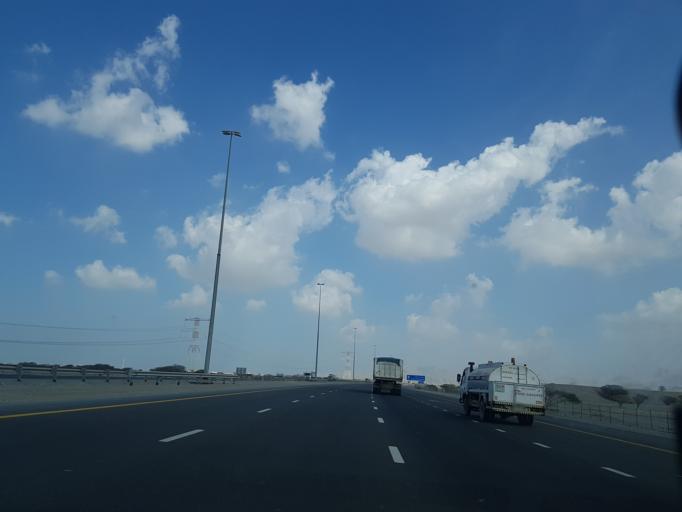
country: AE
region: Ra's al Khaymah
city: Ras al-Khaimah
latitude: 25.7500
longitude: 56.0170
